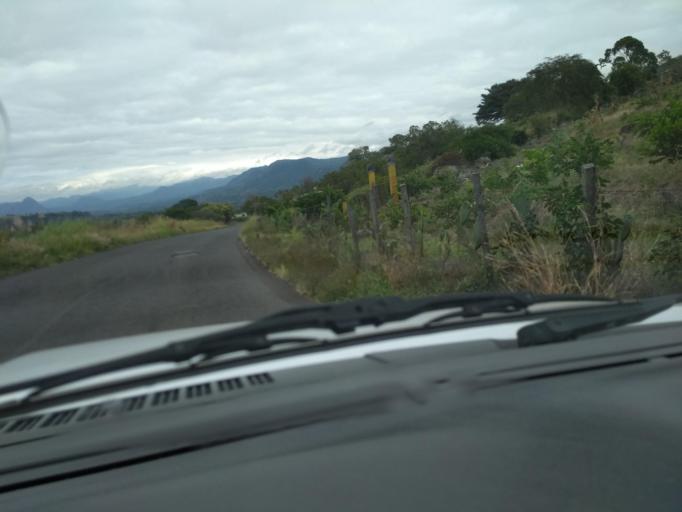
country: MX
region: Veracruz
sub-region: Actopan
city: Trapiche del Rosario
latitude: 19.5838
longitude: -96.7965
